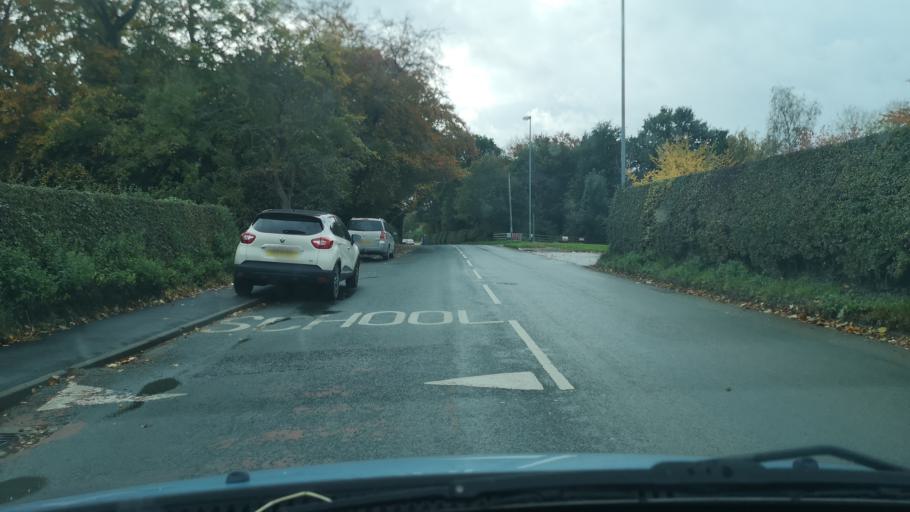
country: GB
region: England
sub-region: City and Borough of Wakefield
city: Fitzwilliam
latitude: 53.6490
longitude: -1.3857
